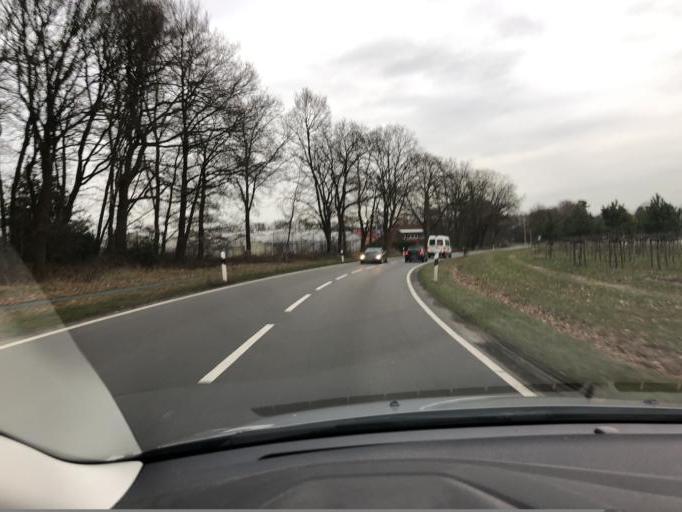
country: DE
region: Lower Saxony
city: Wiefelstede
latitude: 53.1934
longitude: 8.1239
